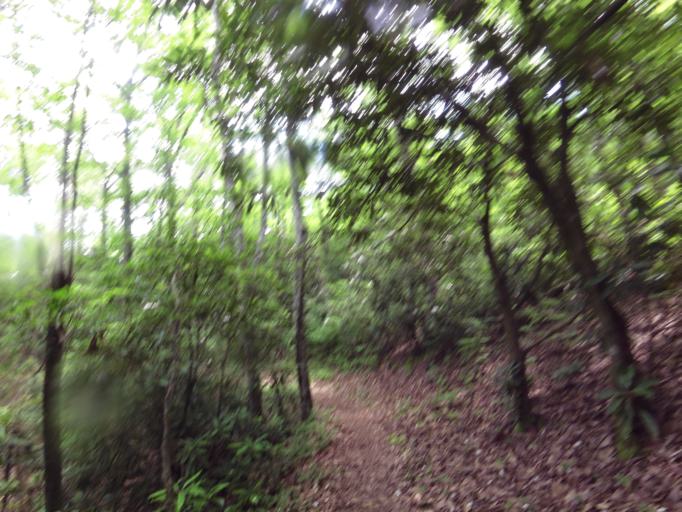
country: US
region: Tennessee
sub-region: Blount County
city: Wildwood
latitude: 35.6505
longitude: -83.8189
